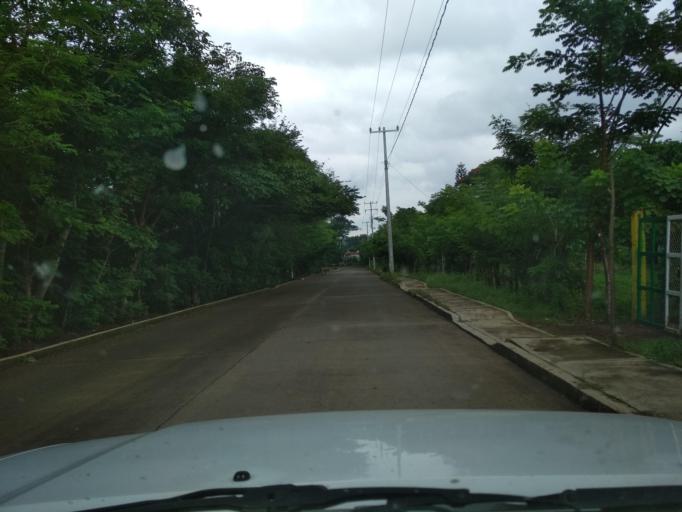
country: MX
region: Veracruz
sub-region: San Andres Tuxtla
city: El Huidero
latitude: 18.3917
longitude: -95.1931
